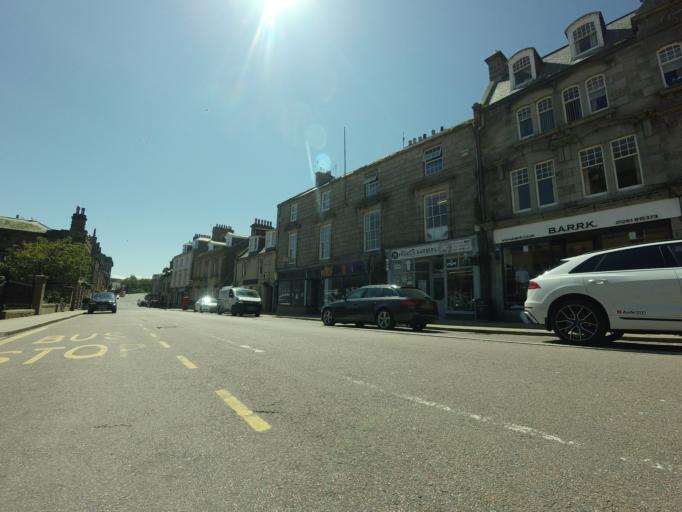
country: GB
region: Scotland
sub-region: Aberdeenshire
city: Banff
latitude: 57.6644
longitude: -2.5217
